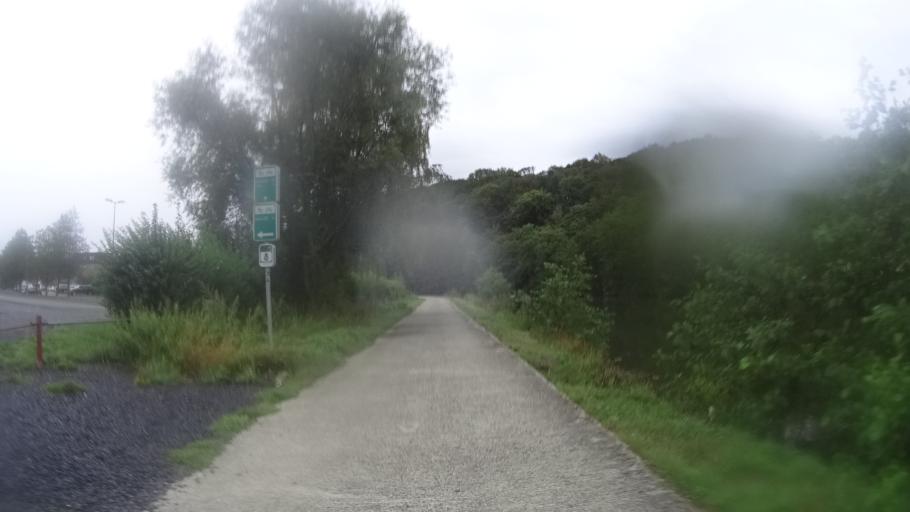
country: BE
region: Wallonia
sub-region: Province du Hainaut
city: Lobbes
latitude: 50.3466
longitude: 4.2568
